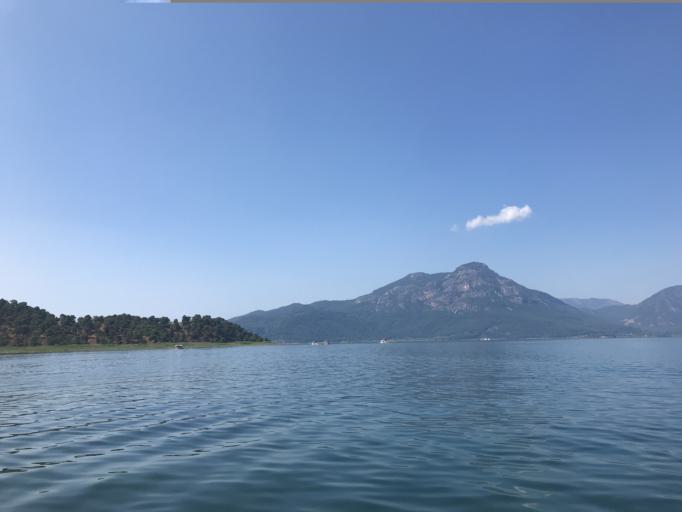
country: TR
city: Dalyan
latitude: 36.9036
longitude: 28.6474
